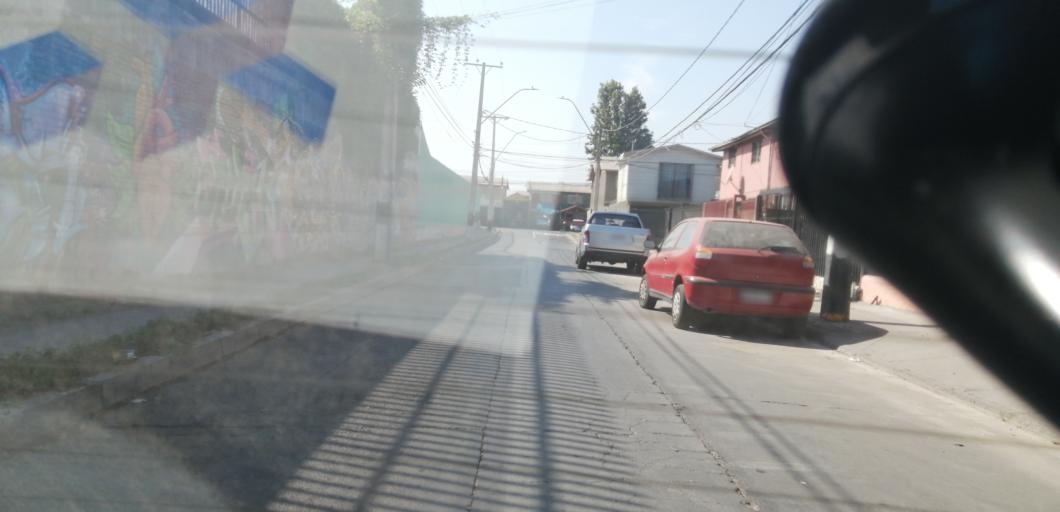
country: CL
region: Santiago Metropolitan
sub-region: Provincia de Santiago
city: Lo Prado
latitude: -33.4583
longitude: -70.7465
